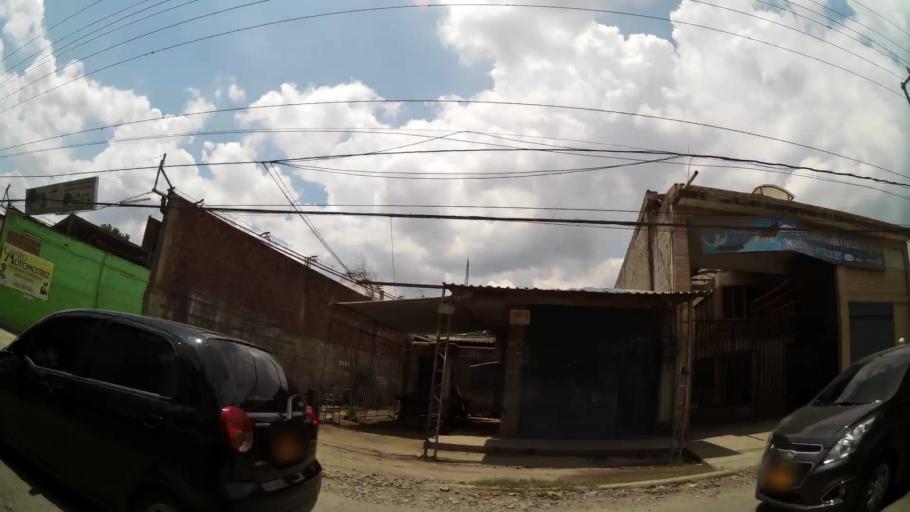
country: CO
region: Valle del Cauca
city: Cali
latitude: 3.4530
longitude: -76.4720
